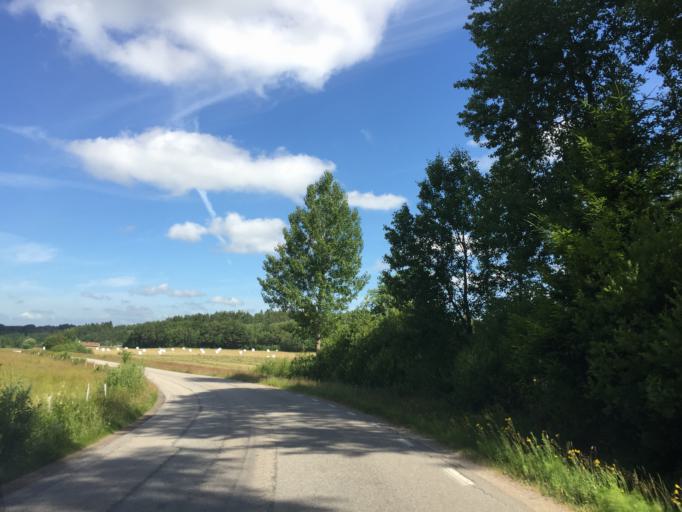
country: SE
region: Vaestra Goetaland
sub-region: Orust
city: Henan
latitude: 58.2870
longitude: 11.5833
